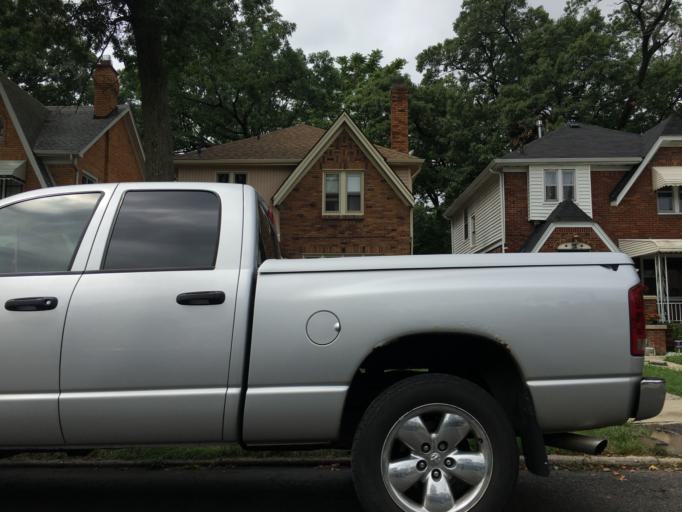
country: US
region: Michigan
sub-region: Oakland County
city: Ferndale
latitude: 42.4117
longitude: -83.1522
